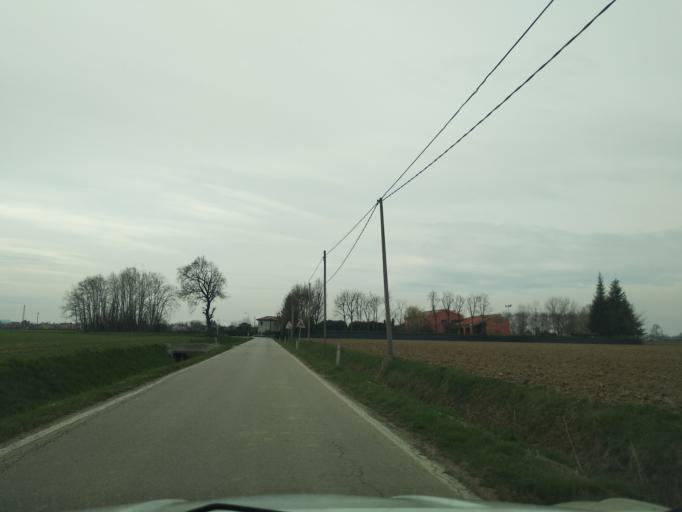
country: IT
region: Veneto
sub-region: Provincia di Padova
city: Selvazzano Dentro
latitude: 45.4031
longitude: 11.7931
